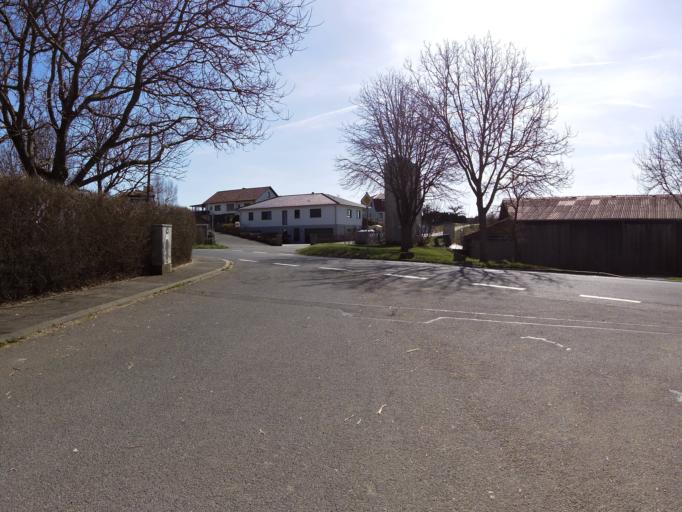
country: DE
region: Bavaria
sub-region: Regierungsbezirk Unterfranken
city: Biebelried
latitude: 49.7954
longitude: 10.1085
